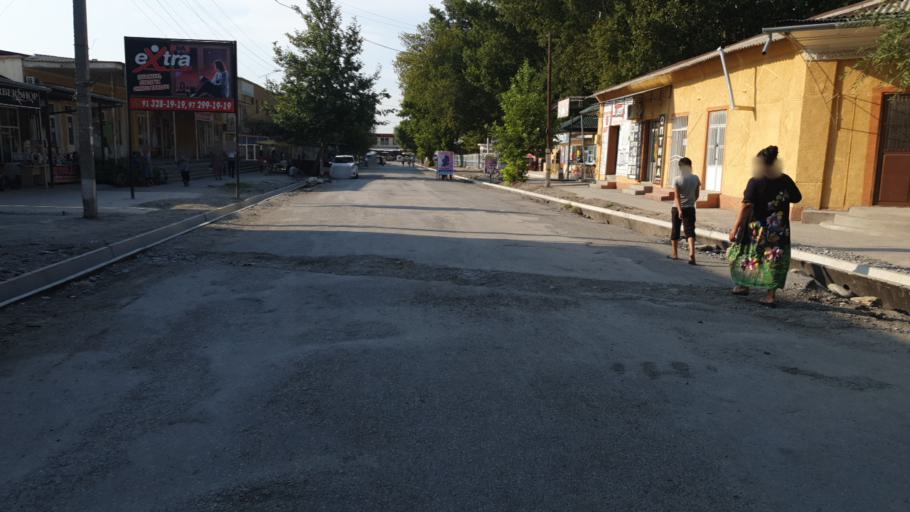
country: UZ
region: Fergana
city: Yaypan
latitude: 40.3789
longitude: 70.8108
